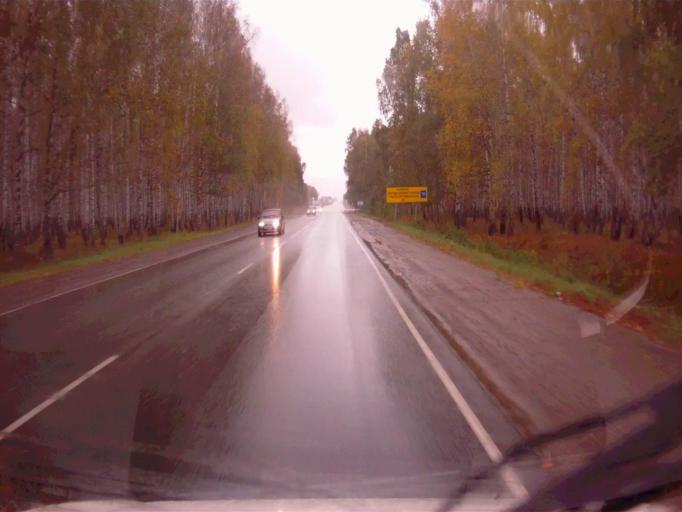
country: RU
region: Chelyabinsk
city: Argayash
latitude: 55.4146
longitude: 61.0325
